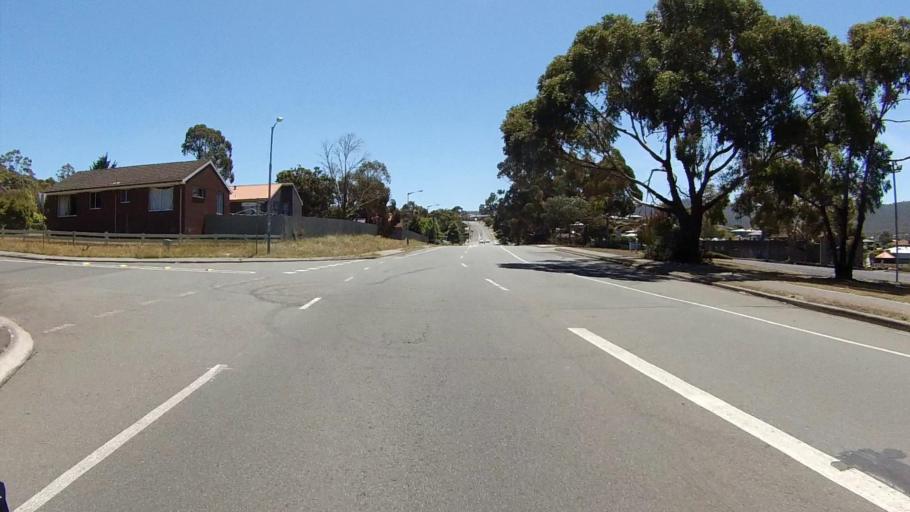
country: AU
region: Tasmania
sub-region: Clarence
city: Rokeby
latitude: -42.8966
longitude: 147.4305
